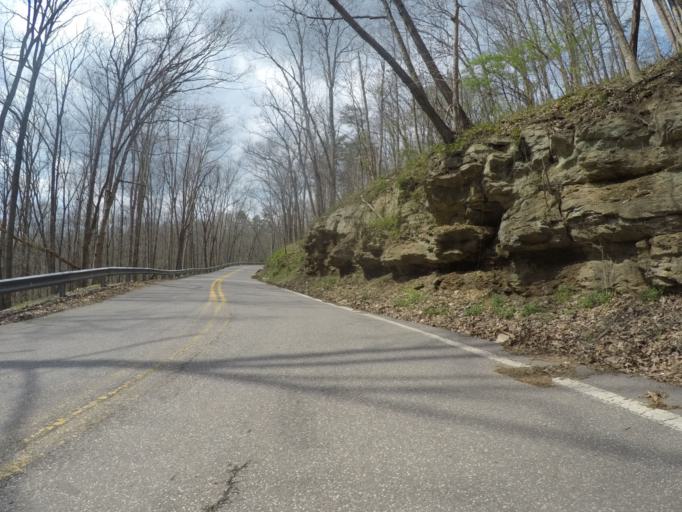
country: US
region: West Virginia
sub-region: Cabell County
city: Pea Ridge
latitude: 38.3509
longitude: -82.3350
